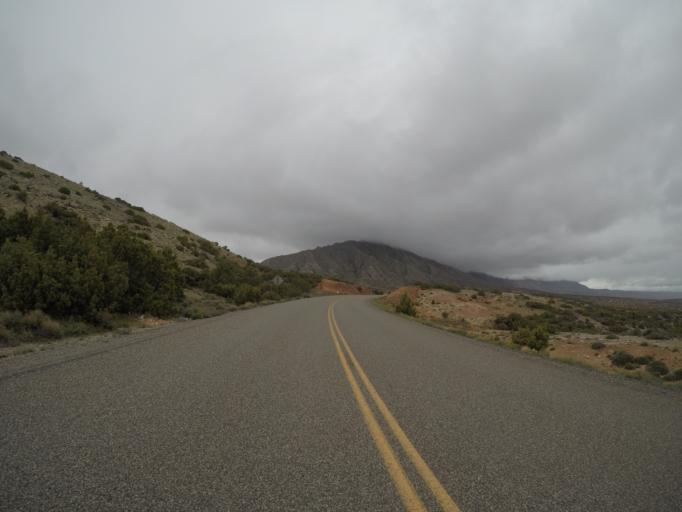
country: US
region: Wyoming
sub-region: Big Horn County
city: Lovell
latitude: 45.0227
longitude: -108.2535
